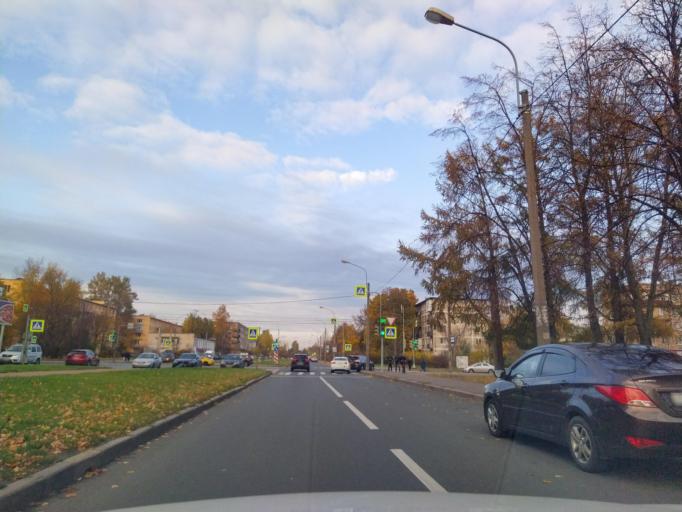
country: RU
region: Leningrad
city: Kalininskiy
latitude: 59.9708
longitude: 30.3970
